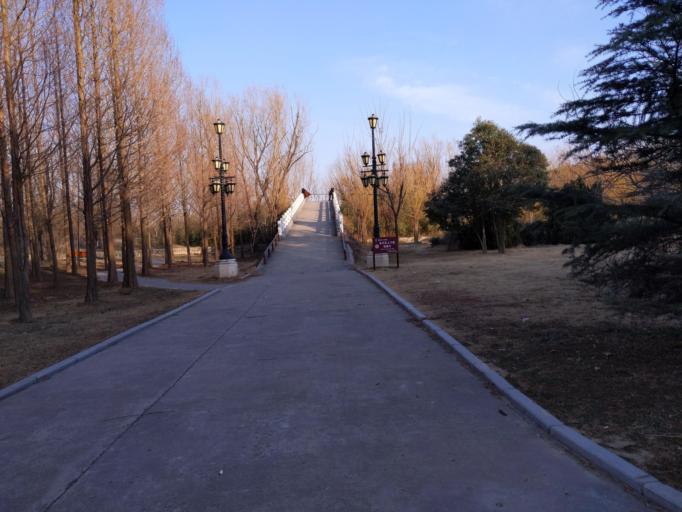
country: CN
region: Henan Sheng
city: Puyang
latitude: 35.7801
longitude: 114.9516
